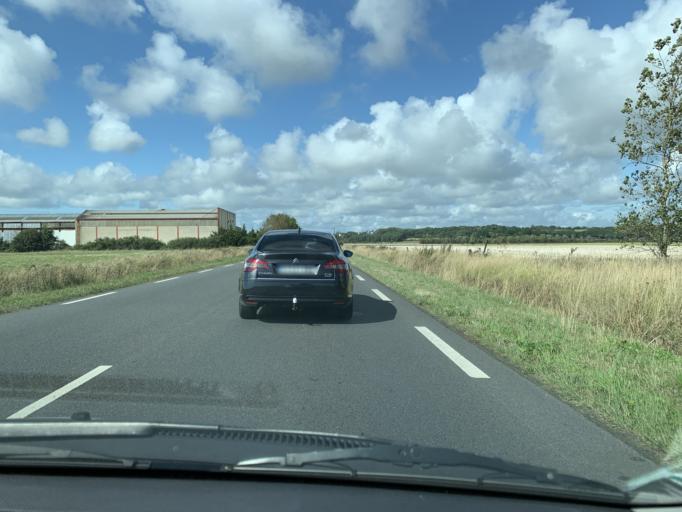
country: FR
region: Pays de la Loire
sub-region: Departement de la Loire-Atlantique
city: Guerande
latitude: 47.3055
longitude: -2.4305
